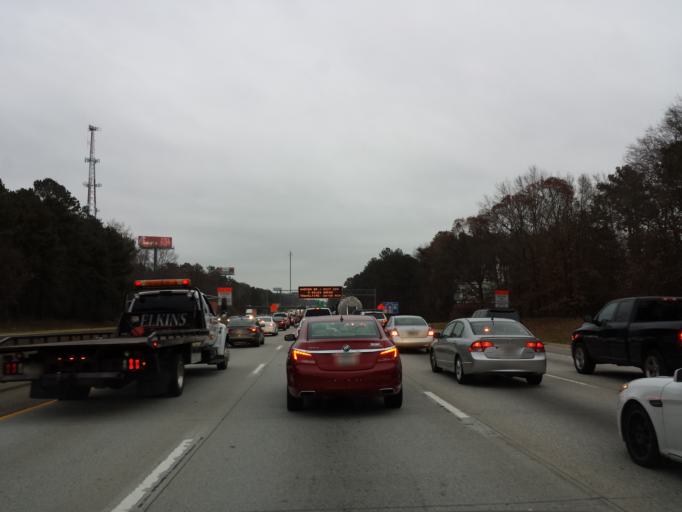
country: US
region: Georgia
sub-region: Clayton County
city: Morrow
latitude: 33.5560
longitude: -84.3036
